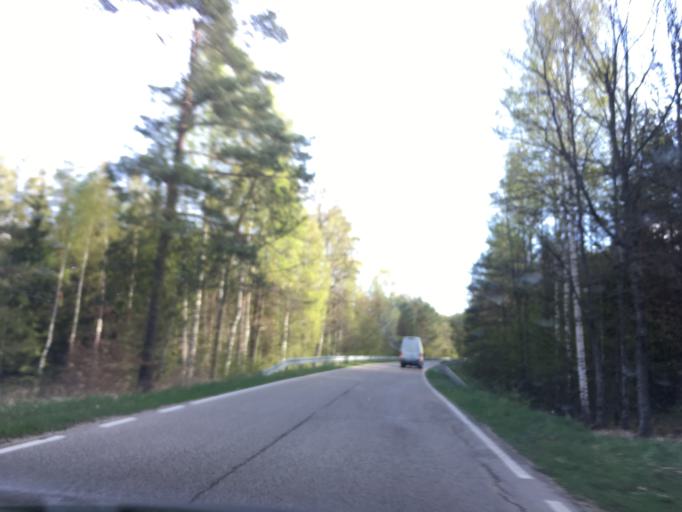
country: PL
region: Warmian-Masurian Voivodeship
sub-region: Powiat piski
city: Ruciane-Nida
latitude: 53.6718
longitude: 21.5773
